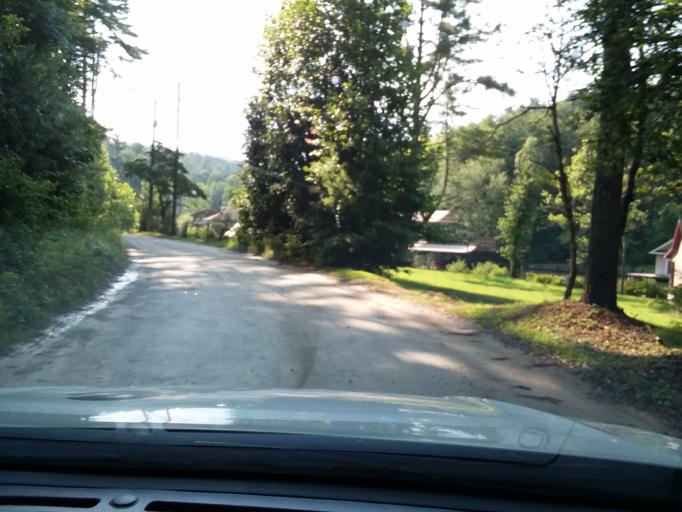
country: US
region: Georgia
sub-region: Habersham County
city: Clarkesville
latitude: 34.7531
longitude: -83.4925
